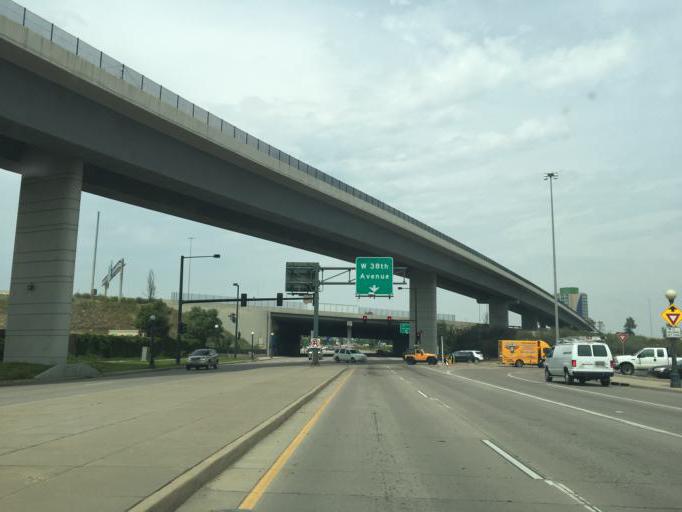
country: US
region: Colorado
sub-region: Denver County
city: Denver
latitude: 39.7666
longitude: -104.9949
